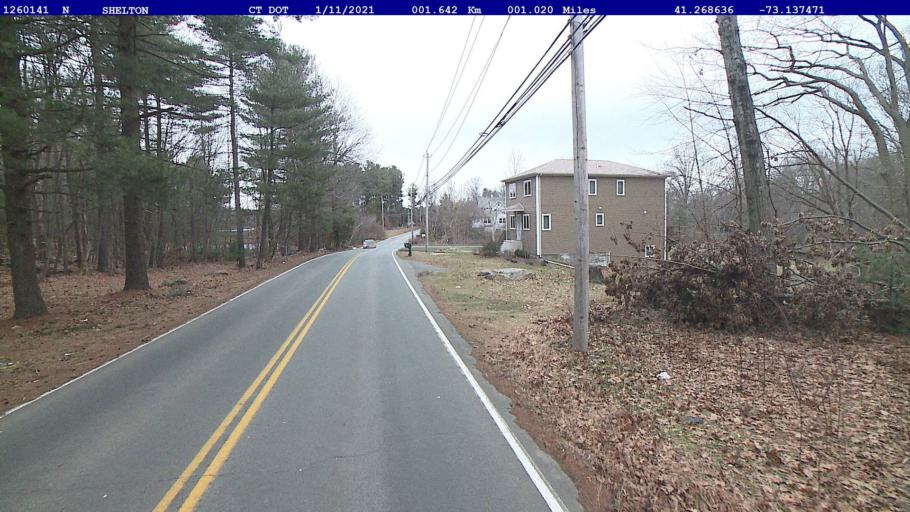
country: US
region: Connecticut
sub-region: Fairfield County
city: Shelton
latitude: 41.2687
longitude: -73.1375
